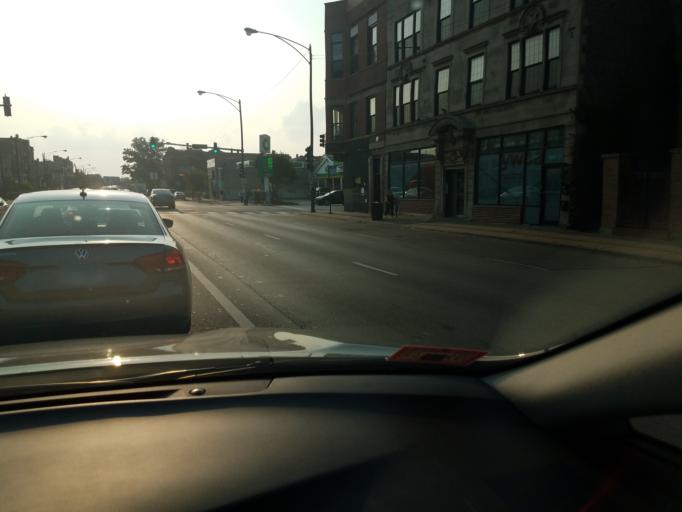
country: US
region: Illinois
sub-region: Cook County
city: Lincolnwood
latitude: 41.9249
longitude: -87.6968
